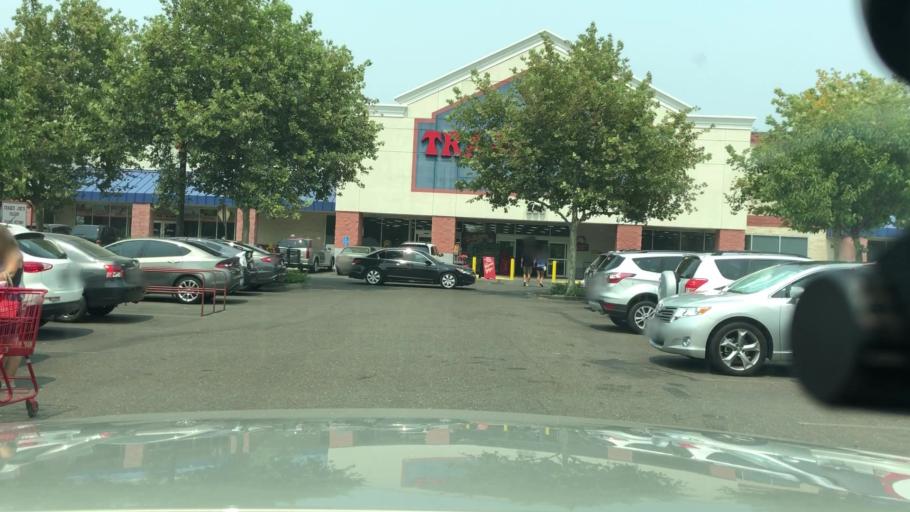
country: US
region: California
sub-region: Sacramento County
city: Folsom
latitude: 38.6719
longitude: -121.1559
